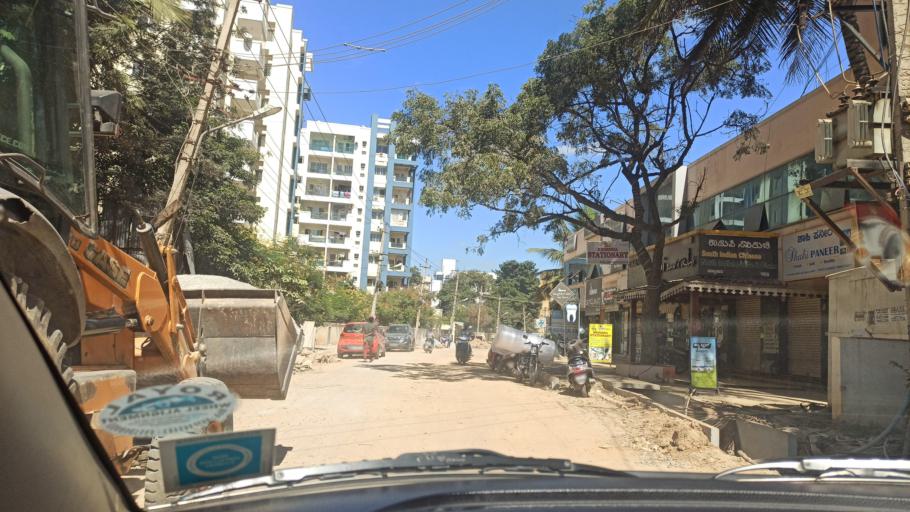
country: IN
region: Karnataka
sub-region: Bangalore Urban
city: Bangalore
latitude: 12.9216
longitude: 77.6717
